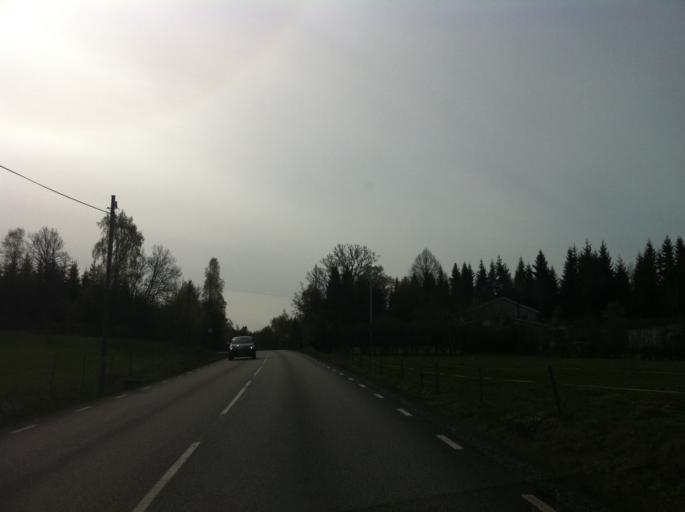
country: SE
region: Vaestra Goetaland
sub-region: Marks Kommun
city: Kinna
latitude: 57.4319
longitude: 12.7587
